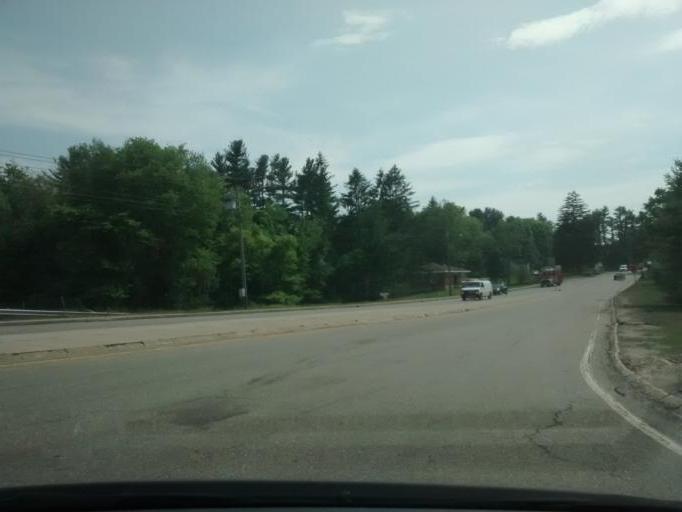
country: US
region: Massachusetts
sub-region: Bristol County
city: Norton Center
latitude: 41.9811
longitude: -71.1609
